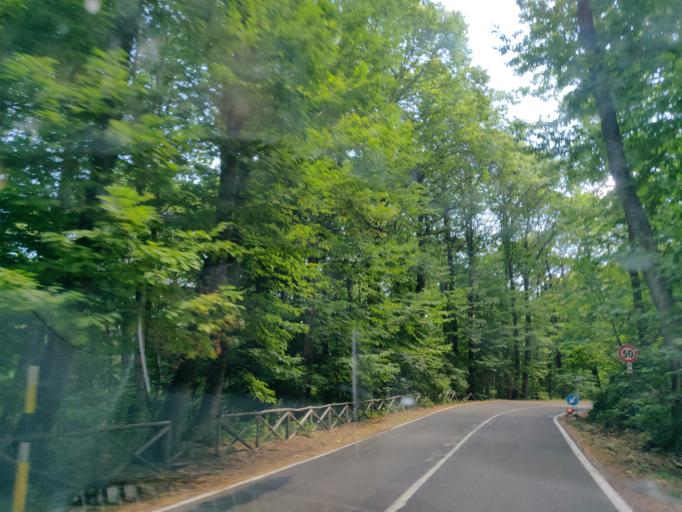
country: IT
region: Tuscany
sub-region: Provincia di Siena
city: Abbadia San Salvatore
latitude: 42.8968
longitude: 11.6494
